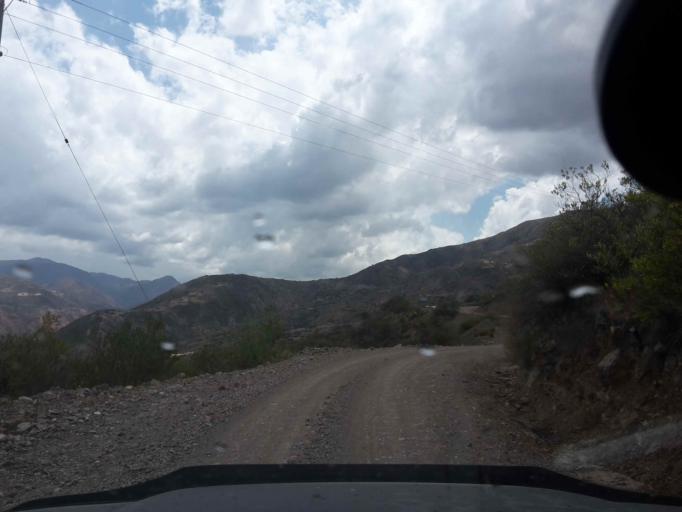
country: BO
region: Cochabamba
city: Sipe Sipe
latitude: -17.5210
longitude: -66.5614
